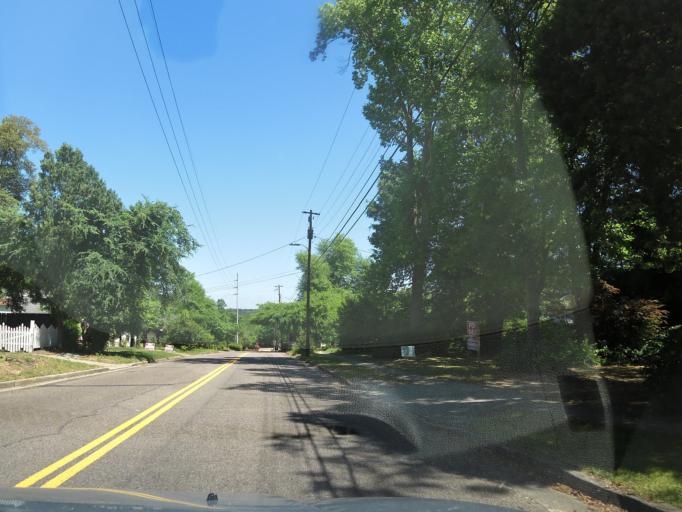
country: US
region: Georgia
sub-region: Richmond County
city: Augusta
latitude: 33.4824
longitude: -82.0266
